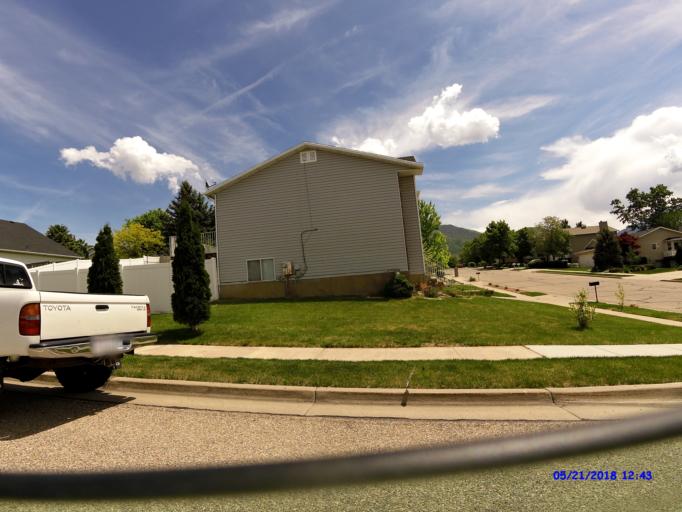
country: US
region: Utah
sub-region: Weber County
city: Washington Terrace
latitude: 41.1722
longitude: -111.9546
